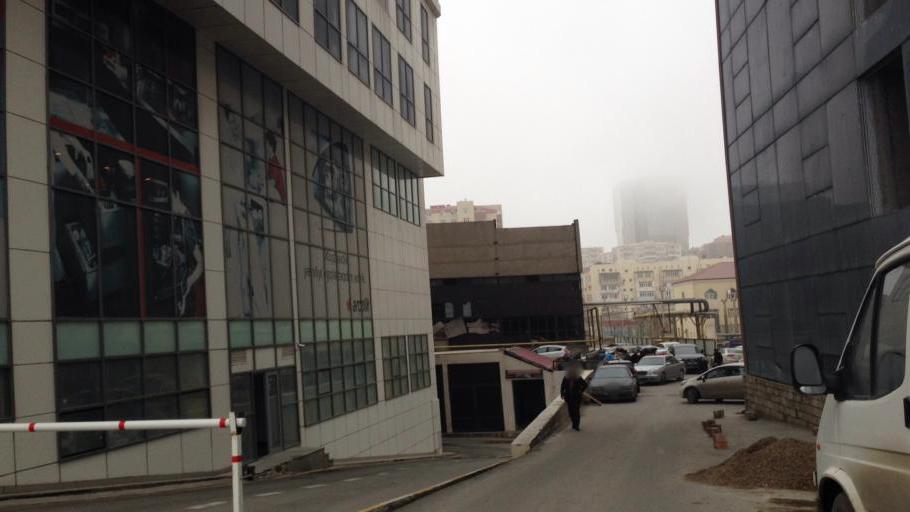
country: AZ
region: Baki
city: Baku
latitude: 40.3883
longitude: 49.8719
